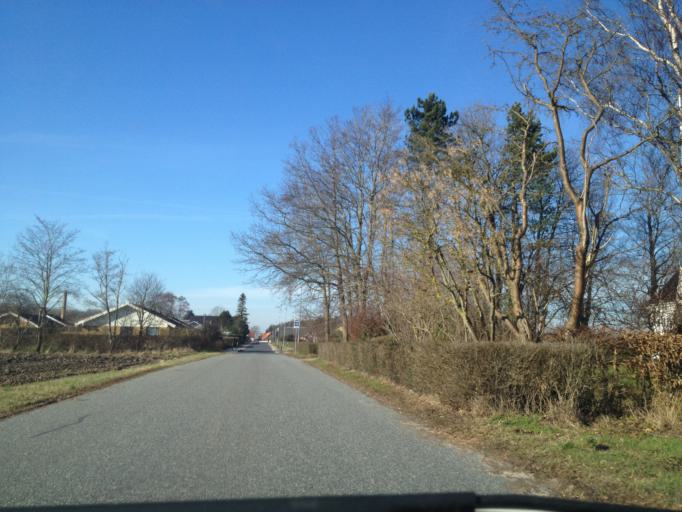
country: DK
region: South Denmark
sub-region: Nyborg Kommune
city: Ullerslev
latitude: 55.3931
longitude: 10.6926
